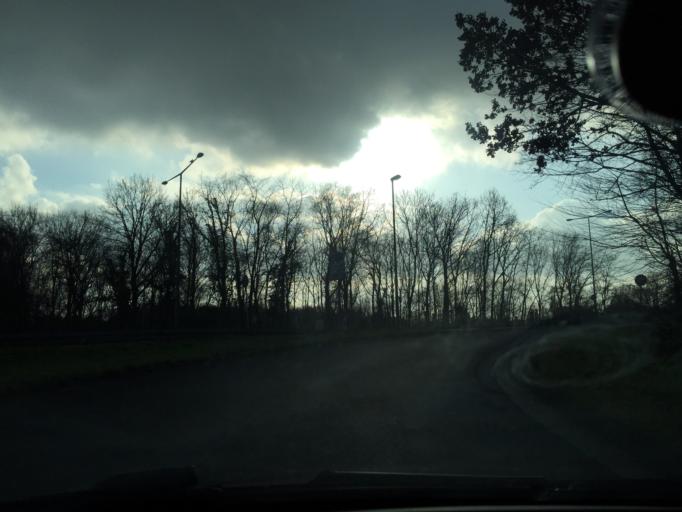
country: DE
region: North Rhine-Westphalia
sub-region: Regierungsbezirk Koln
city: Humboldtkolonie
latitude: 50.9310
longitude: 6.9866
